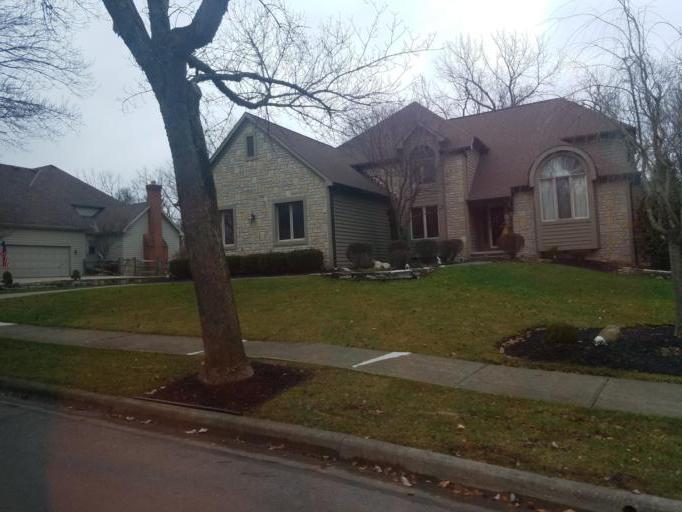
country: US
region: Ohio
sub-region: Franklin County
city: Westerville
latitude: 40.1356
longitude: -82.9540
